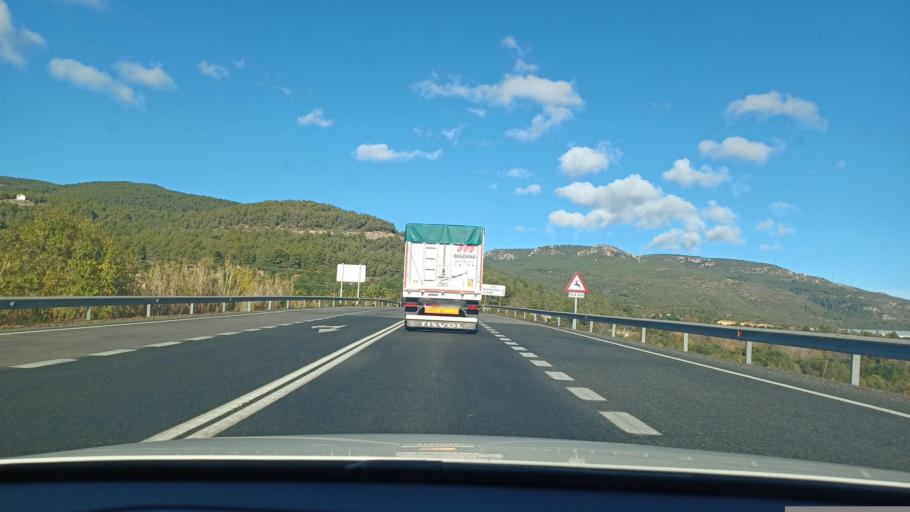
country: ES
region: Catalonia
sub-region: Provincia de Tarragona
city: Alcover
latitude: 41.2651
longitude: 1.1762
